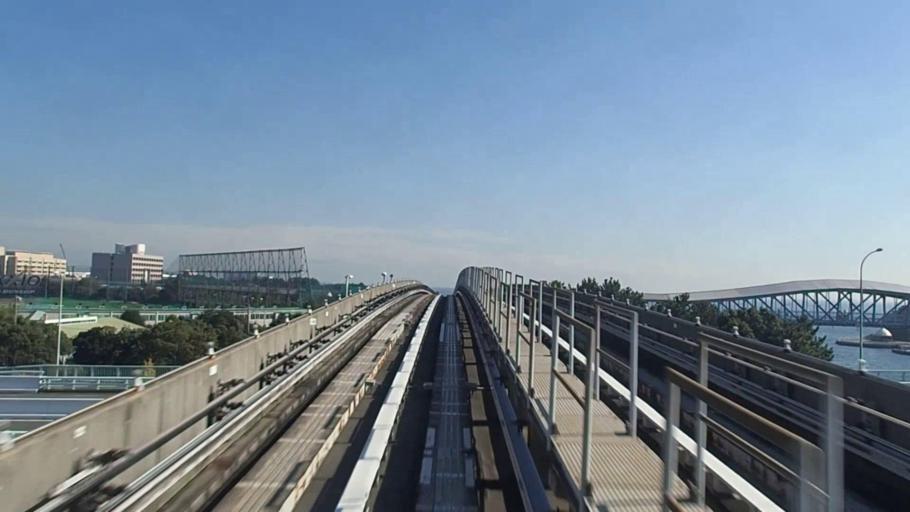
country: JP
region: Kanagawa
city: Yokosuka
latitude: 35.3401
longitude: 139.6443
